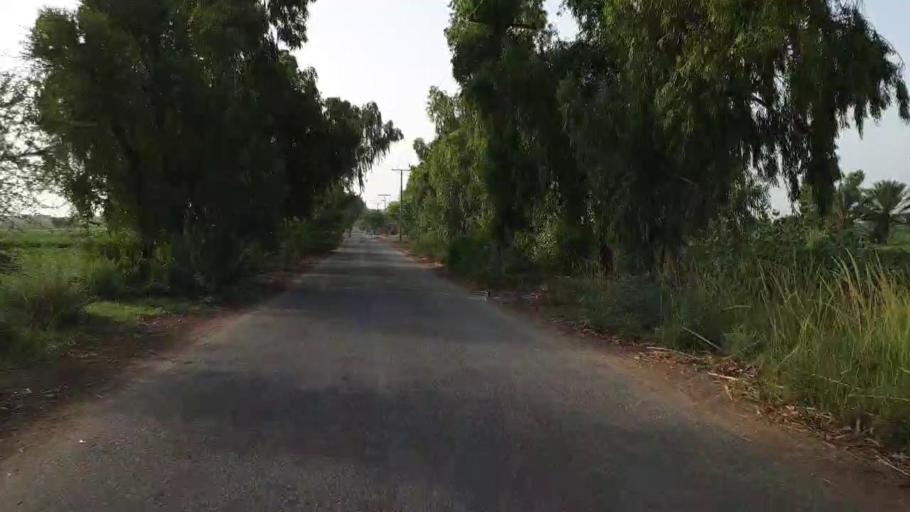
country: PK
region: Sindh
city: Bozdar
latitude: 27.1092
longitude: 68.9602
